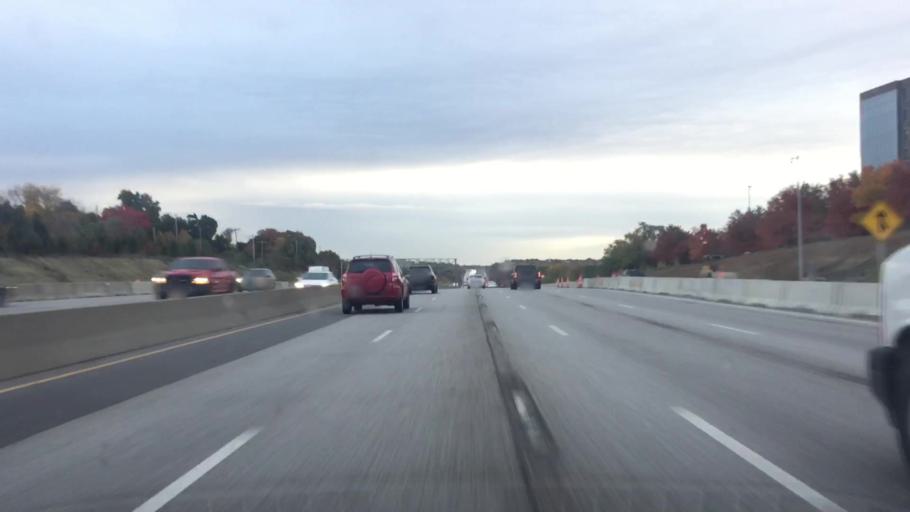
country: US
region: Kansas
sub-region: Johnson County
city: Leawood
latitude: 38.9336
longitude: -94.6147
